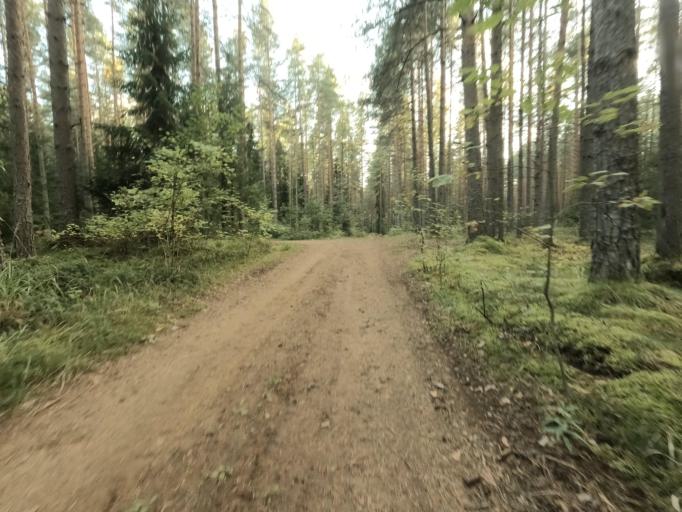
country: RU
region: Leningrad
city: Otradnoye
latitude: 59.8340
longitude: 30.7641
